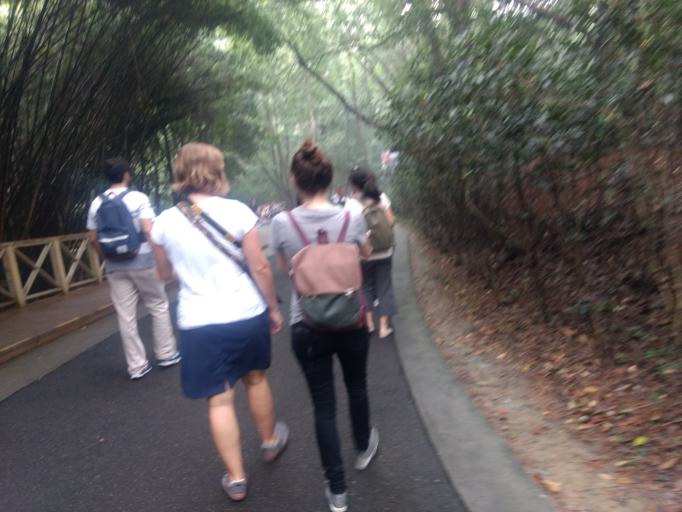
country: CN
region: Sichuan
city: Xindu
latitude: 30.7390
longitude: 104.1402
